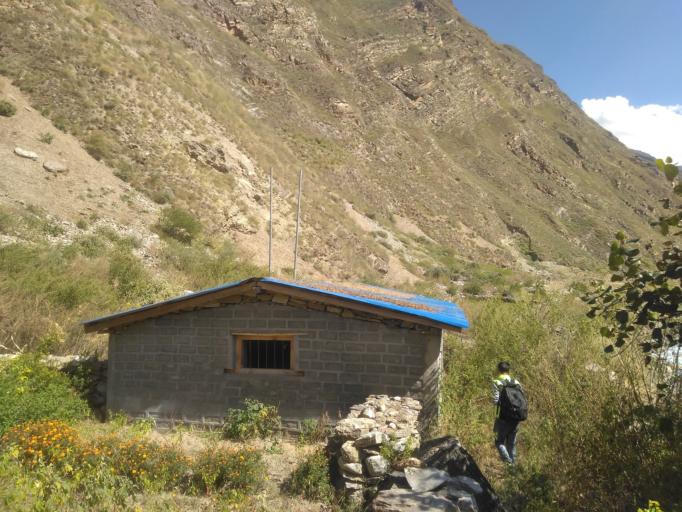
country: NP
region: Western Region
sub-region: Dhawalagiri Zone
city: Jomsom
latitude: 28.9368
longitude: 82.9580
